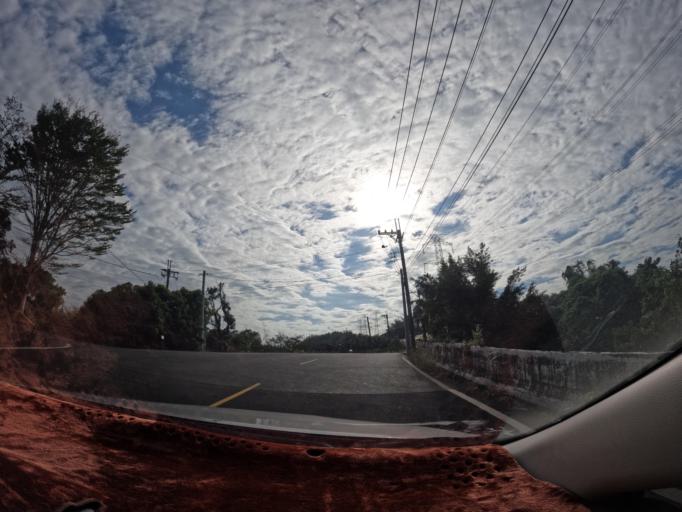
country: TW
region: Taiwan
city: Yujing
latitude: 23.0319
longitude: 120.4150
